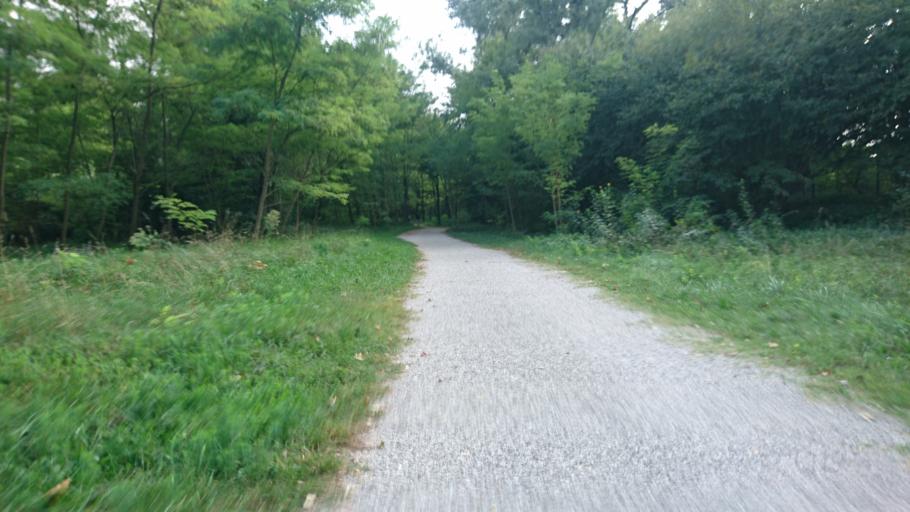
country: IT
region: Veneto
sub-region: Provincia di Padova
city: Grantorto
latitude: 45.5960
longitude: 11.7631
